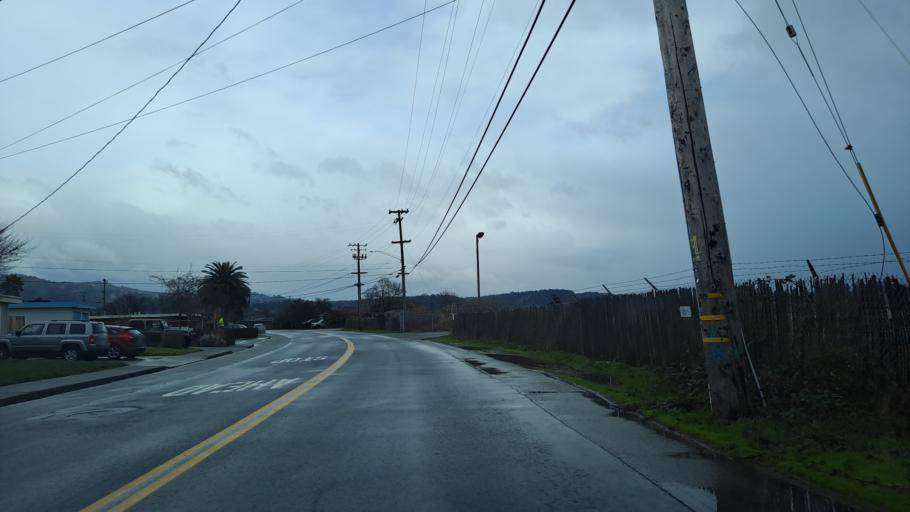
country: US
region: California
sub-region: Humboldt County
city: Fortuna
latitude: 40.5891
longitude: -124.1534
